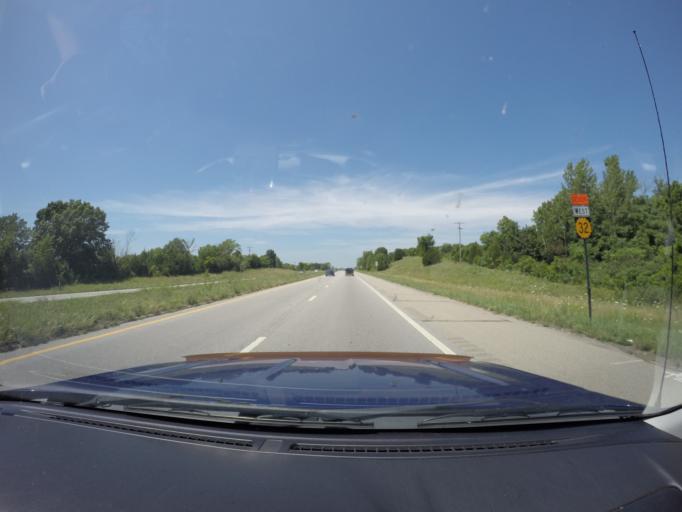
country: US
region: Kansas
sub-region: Wyandotte County
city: Bonner Springs
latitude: 39.1064
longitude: -94.8841
